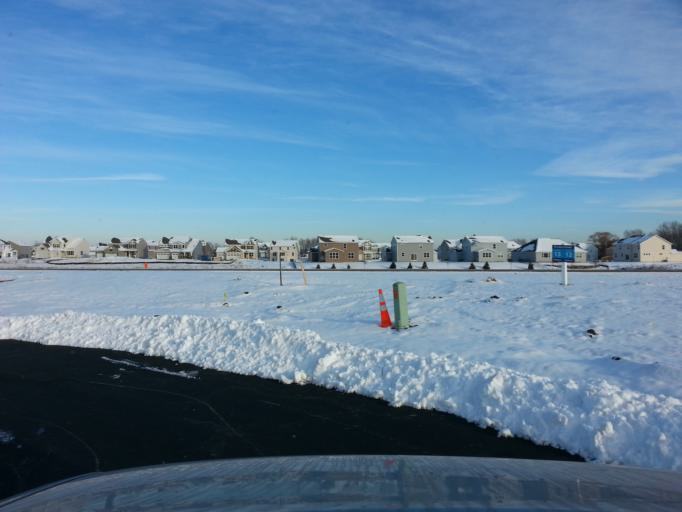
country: US
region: Minnesota
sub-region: Scott County
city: Prior Lake
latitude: 44.7638
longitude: -93.4167
